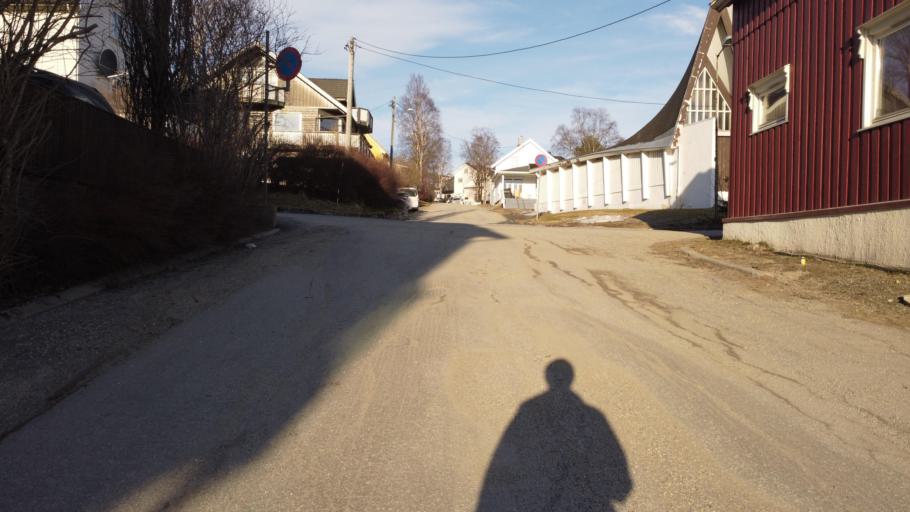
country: NO
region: Nordland
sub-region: Rana
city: Mo i Rana
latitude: 66.3135
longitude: 14.1331
